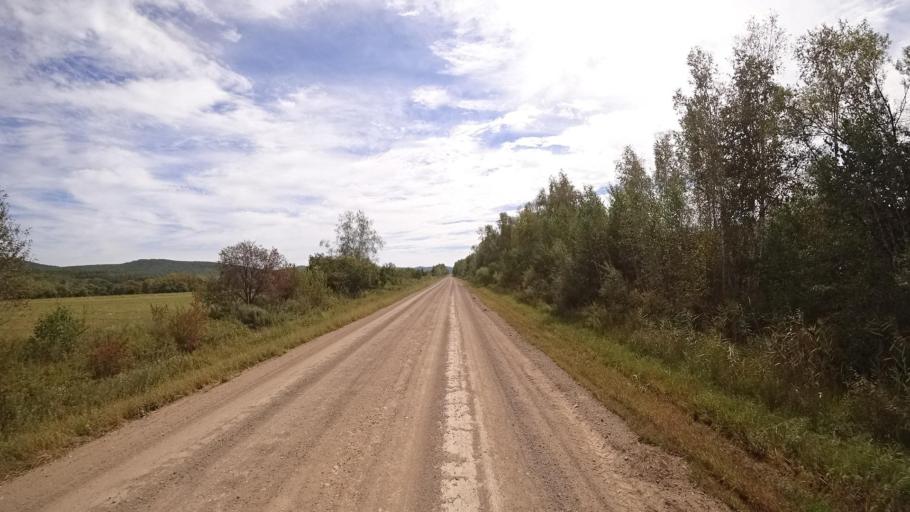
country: RU
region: Primorskiy
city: Yakovlevka
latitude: 44.6149
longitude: 133.5984
